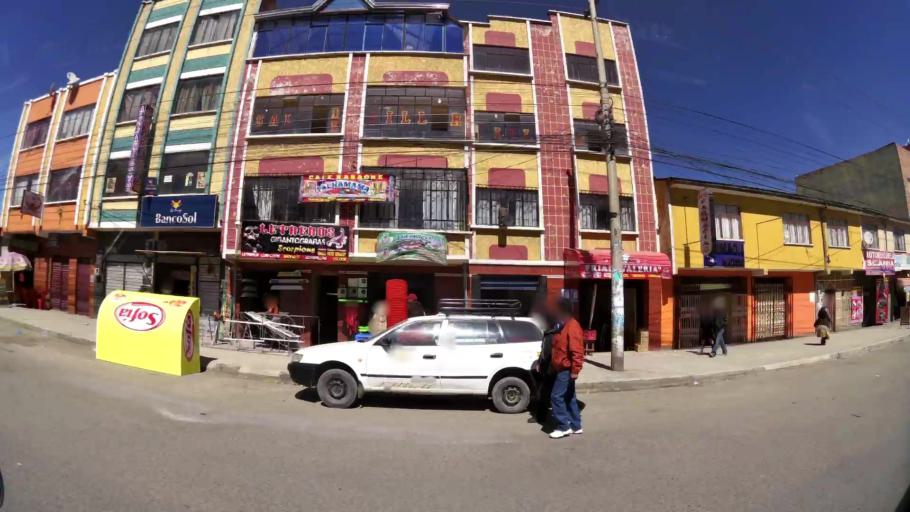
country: BO
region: La Paz
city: La Paz
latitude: -16.4948
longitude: -68.1934
